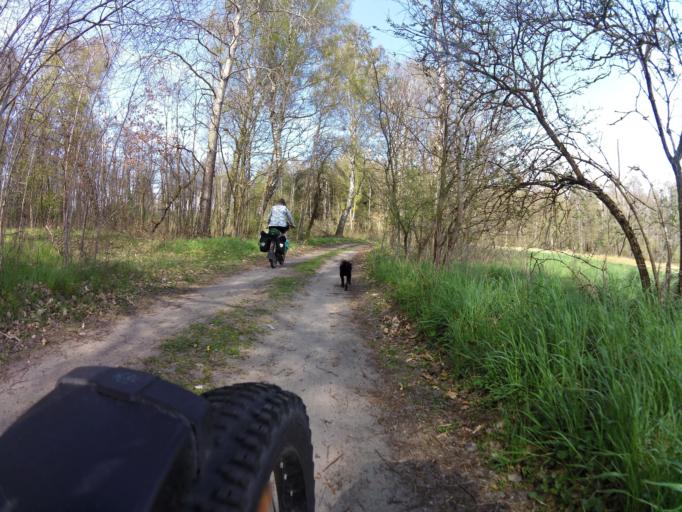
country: PL
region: West Pomeranian Voivodeship
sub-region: Powiat lobeski
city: Resko
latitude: 53.8059
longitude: 15.4449
